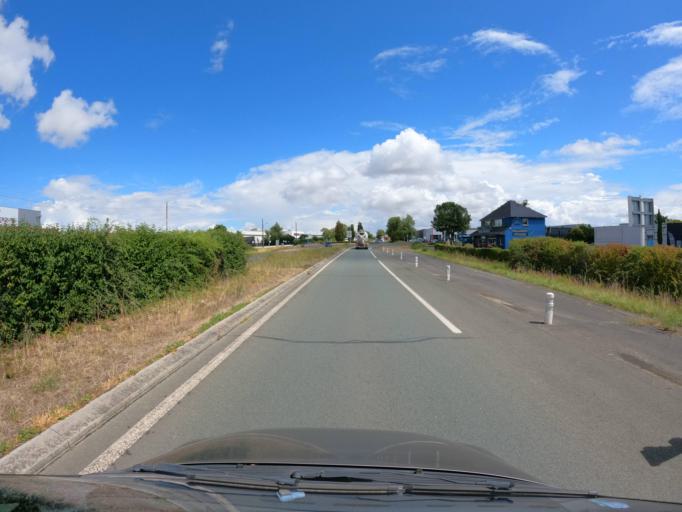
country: FR
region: Pays de la Loire
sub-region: Departement de Maine-et-Loire
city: Avrille
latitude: 47.5173
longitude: -0.6146
